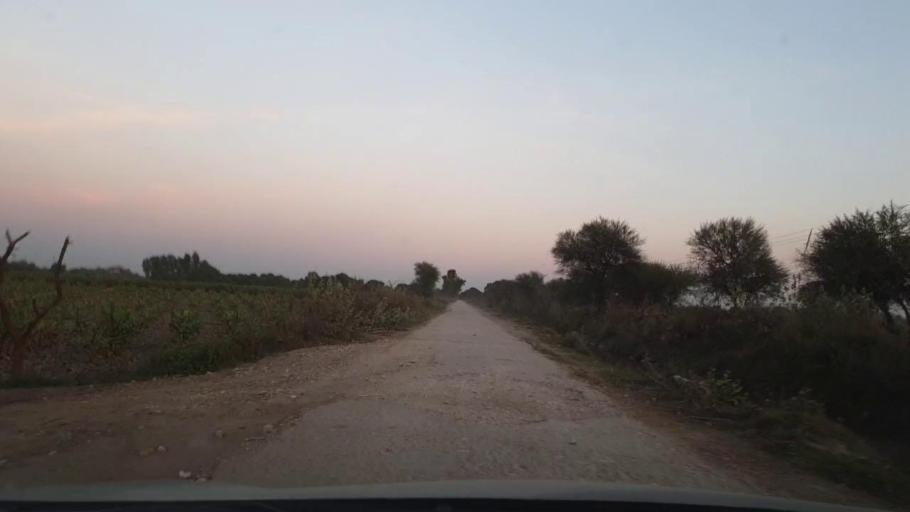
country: PK
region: Sindh
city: Tando Allahyar
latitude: 25.5566
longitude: 68.7834
